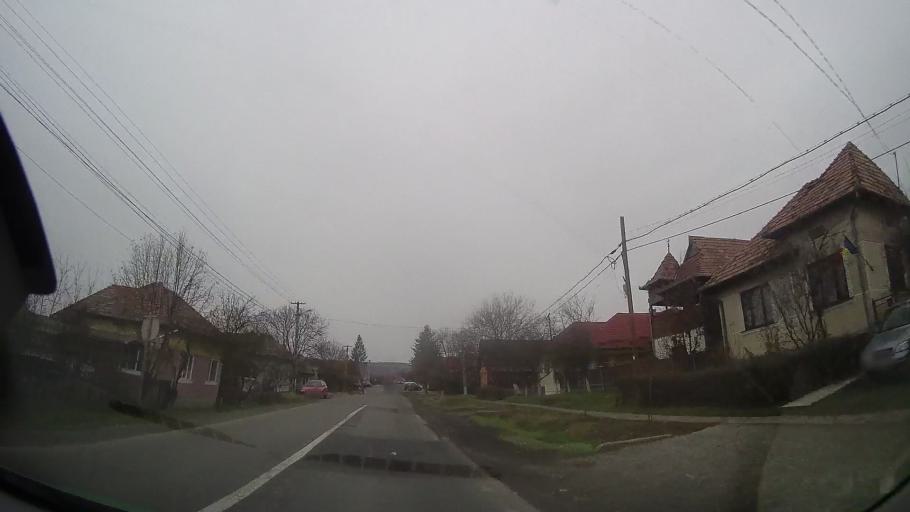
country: RO
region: Mures
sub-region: Comuna Ceausu de Campie
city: Ceausu de Campie
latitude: 46.6445
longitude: 24.5008
